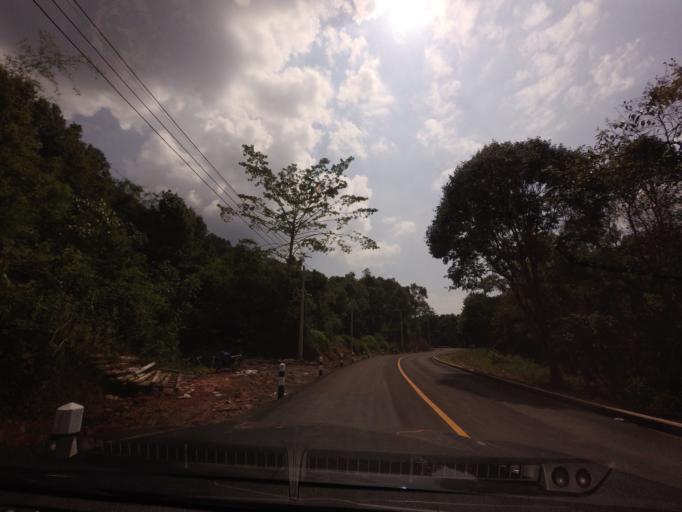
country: TH
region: Nan
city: Bo Kluea
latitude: 19.1890
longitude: 101.1806
